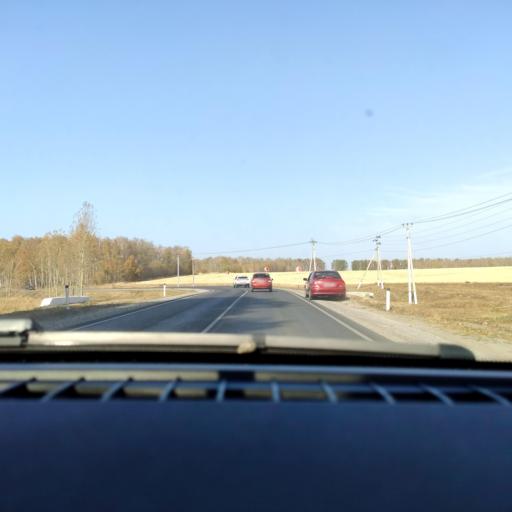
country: RU
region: Voronezj
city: Novaya Usman'
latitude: 51.6782
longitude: 39.4044
